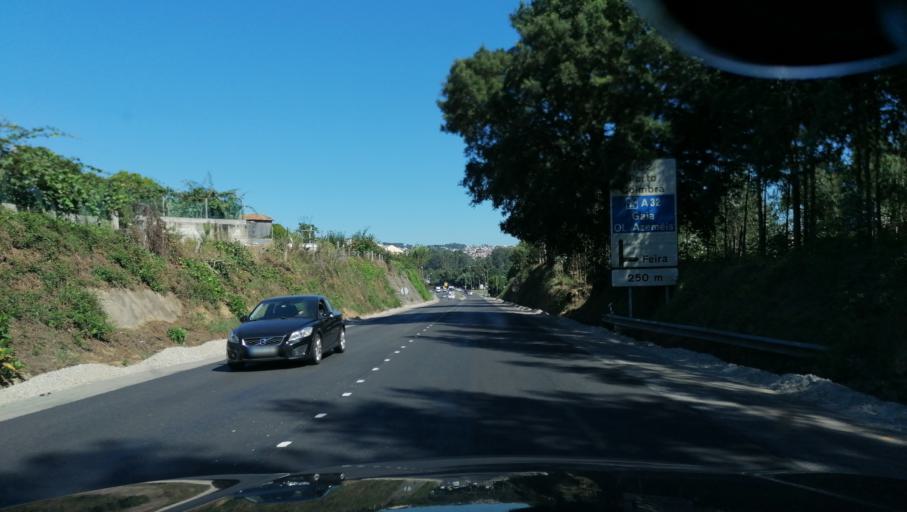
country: PT
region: Aveiro
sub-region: Santa Maria da Feira
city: Feira
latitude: 40.9325
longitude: -8.5400
